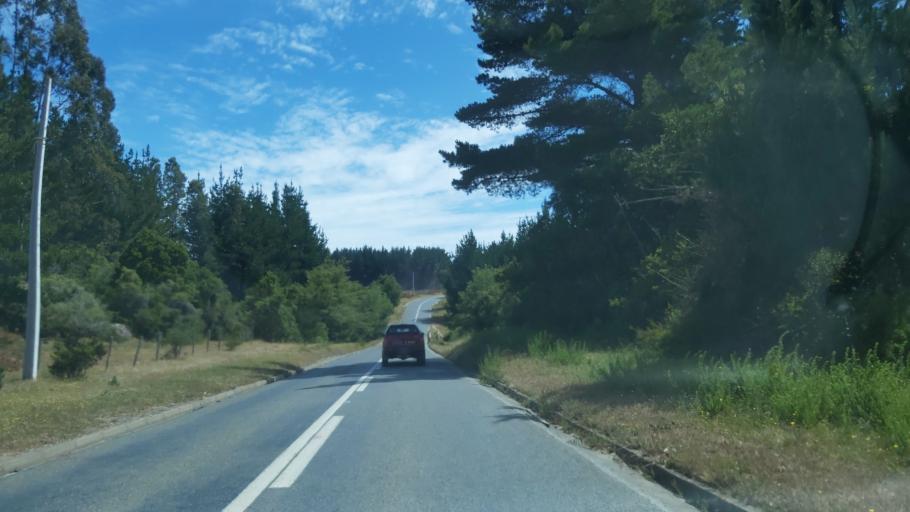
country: CL
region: Maule
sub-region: Provincia de Talca
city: Constitucion
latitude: -35.5482
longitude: -72.5652
